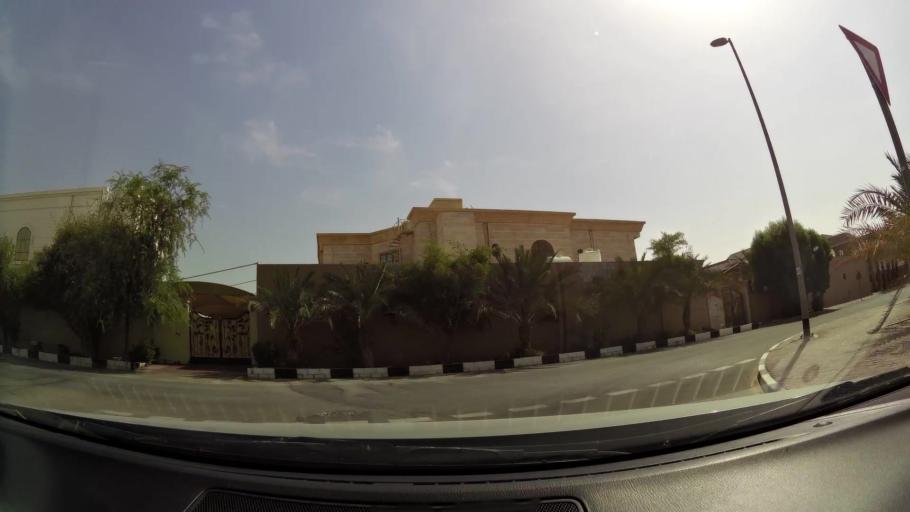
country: AE
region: Ash Shariqah
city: Sharjah
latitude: 25.2039
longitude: 55.4158
